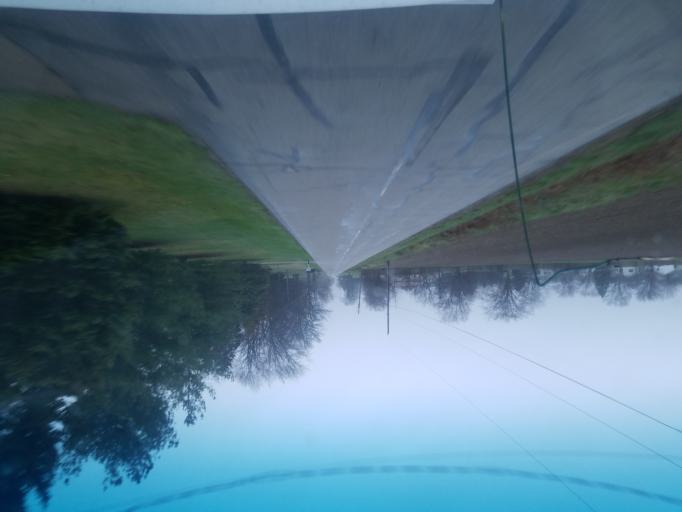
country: US
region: Ohio
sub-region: Henry County
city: Napoleon
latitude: 41.4135
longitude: -84.1929
